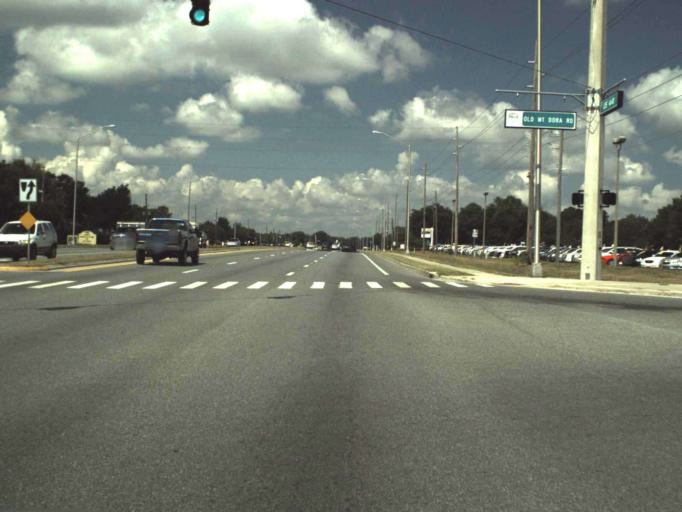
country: US
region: Florida
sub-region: Lake County
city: Mount Dora
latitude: 28.8225
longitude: -81.6636
